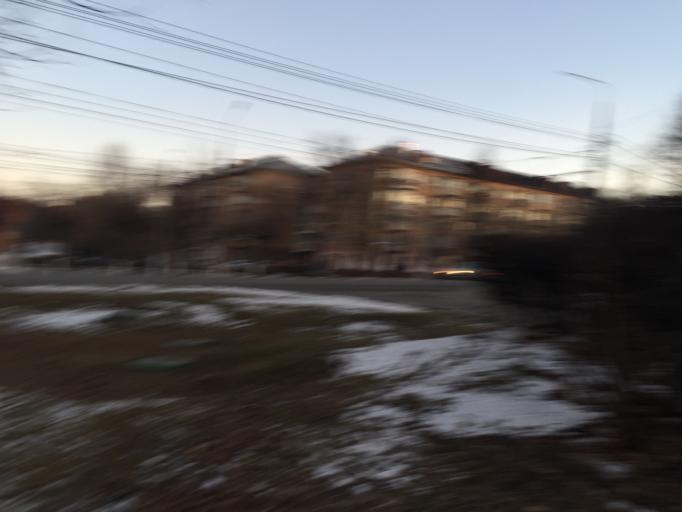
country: RU
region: Tula
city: Mendeleyevskiy
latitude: 54.1624
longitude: 37.5862
